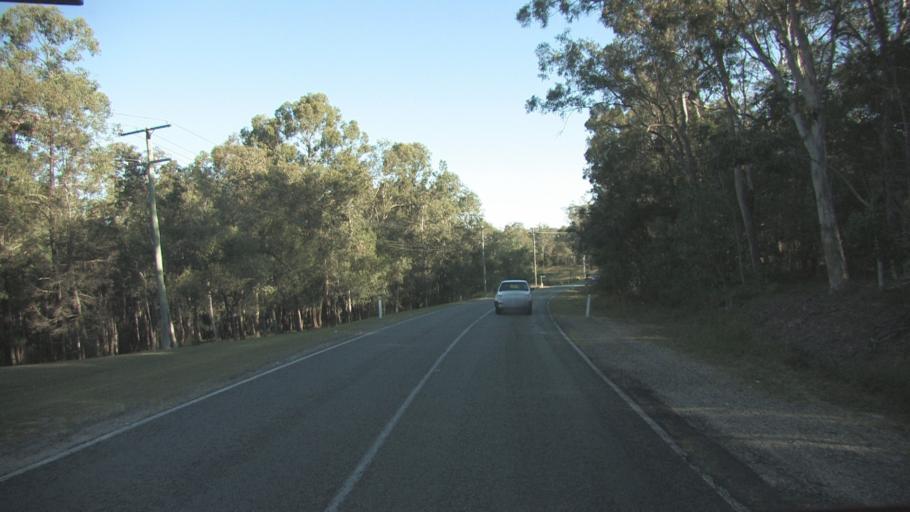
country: AU
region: Queensland
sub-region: Logan
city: Chambers Flat
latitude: -27.7560
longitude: 153.0494
